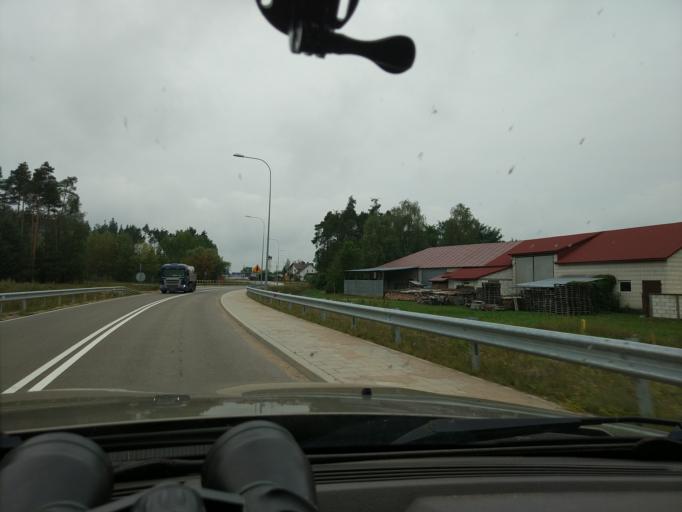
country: PL
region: Podlasie
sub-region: Powiat zambrowski
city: Szumowo
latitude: 52.9137
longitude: 22.0927
